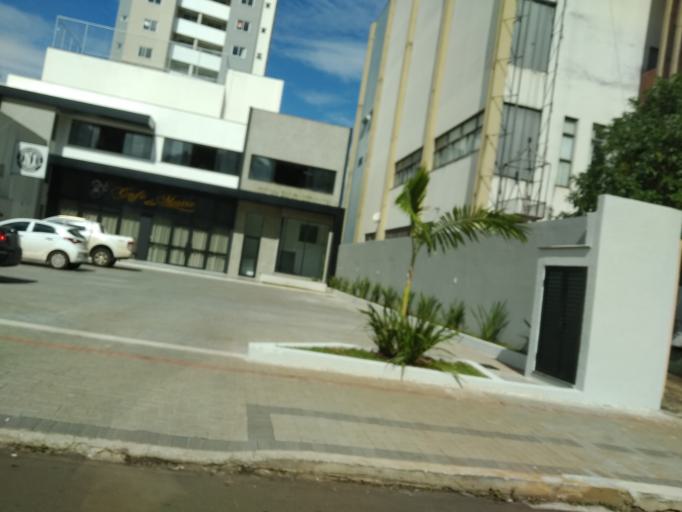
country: BR
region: Parana
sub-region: Pato Branco
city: Pato Branco
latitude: -26.2277
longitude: -52.6741
